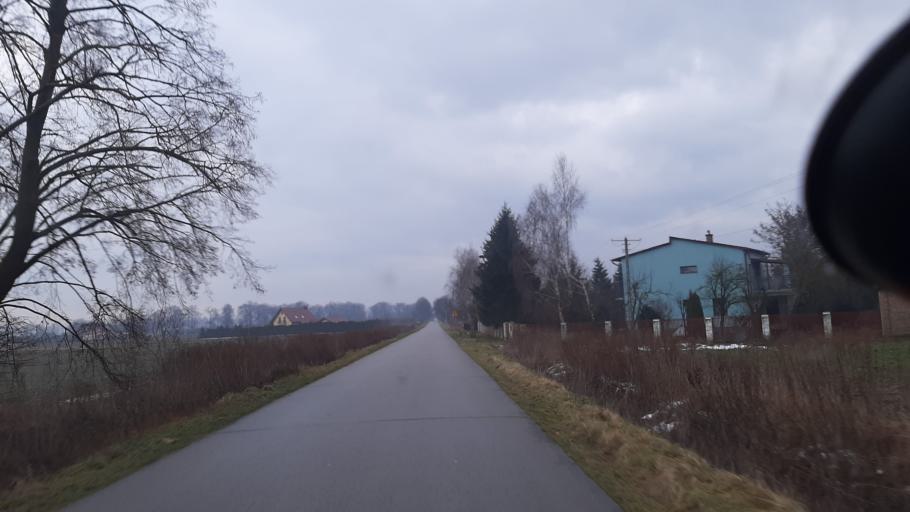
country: PL
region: Lublin Voivodeship
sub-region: Powiat lubelski
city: Lublin
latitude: 51.3372
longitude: 22.5441
